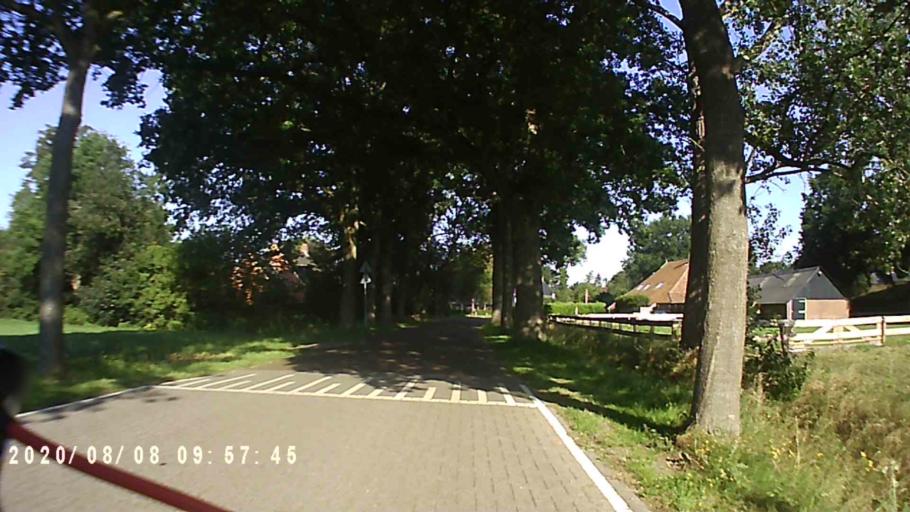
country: NL
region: Groningen
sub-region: Gemeente Leek
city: Leek
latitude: 53.0983
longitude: 6.4090
